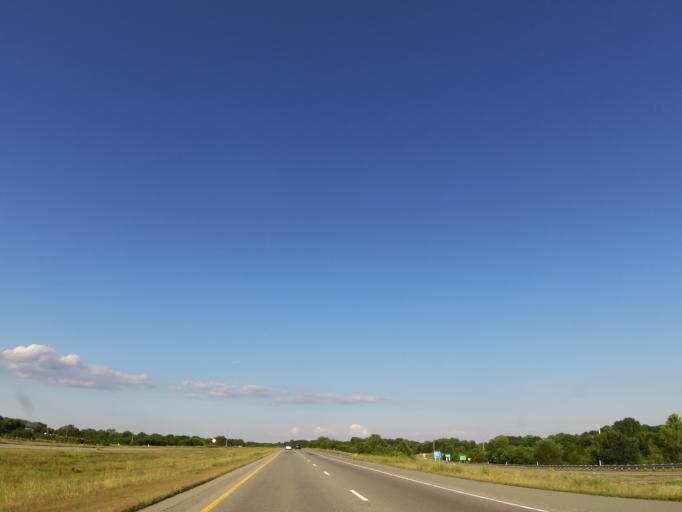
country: US
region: Tennessee
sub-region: Williamson County
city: Nolensville
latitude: 35.8460
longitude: -86.6663
